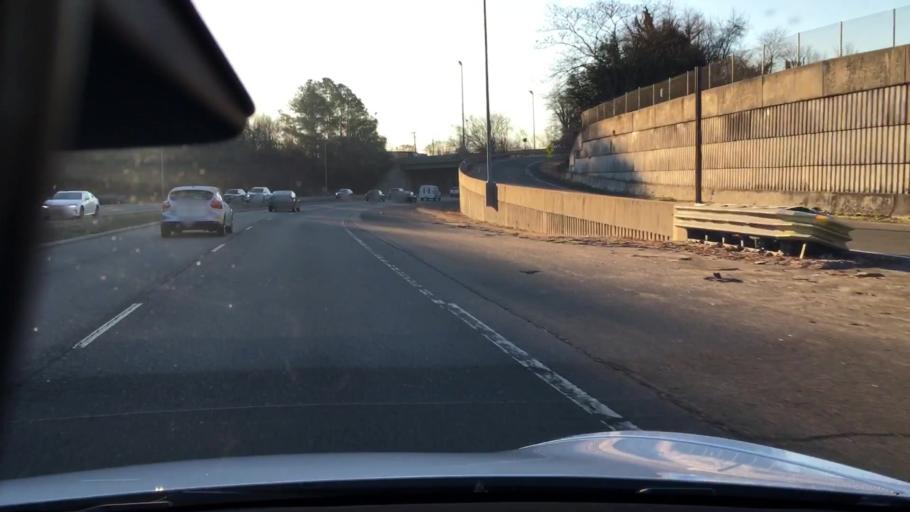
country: US
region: Virginia
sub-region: Chesterfield County
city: Bon Air
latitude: 37.5389
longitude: -77.5304
